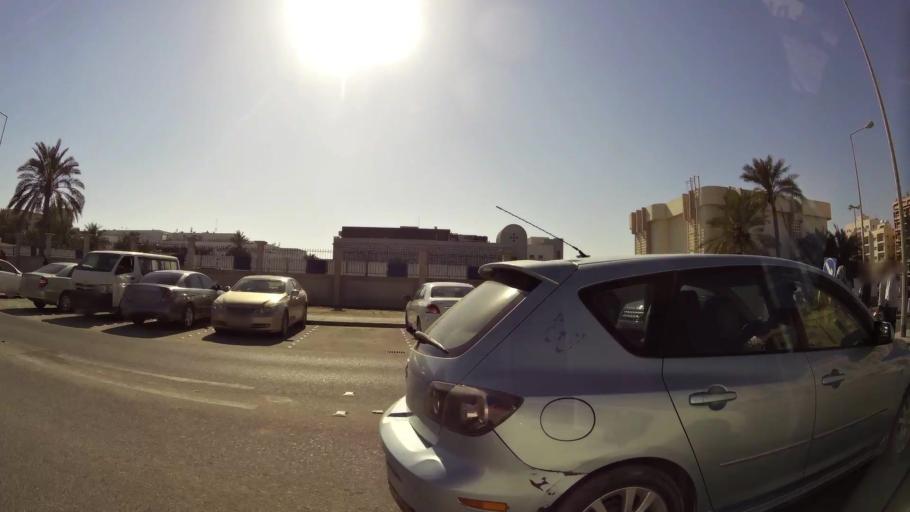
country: BH
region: Manama
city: Manama
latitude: 26.2185
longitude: 50.5740
